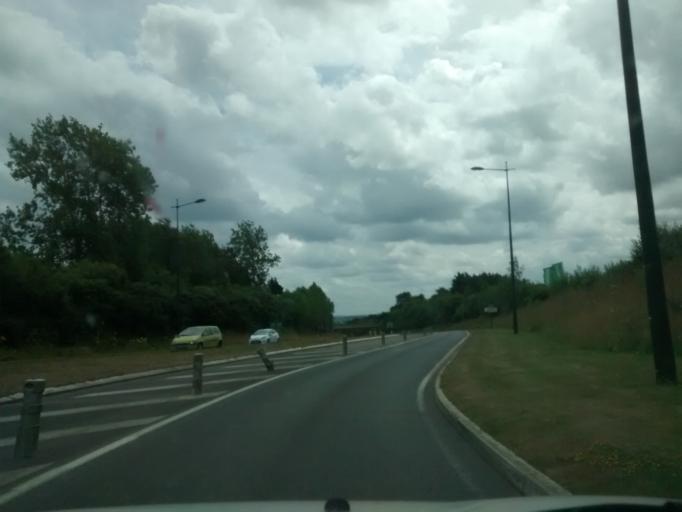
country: FR
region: Brittany
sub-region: Departement des Cotes-d'Armor
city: Lannion
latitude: 48.7509
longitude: -3.4493
